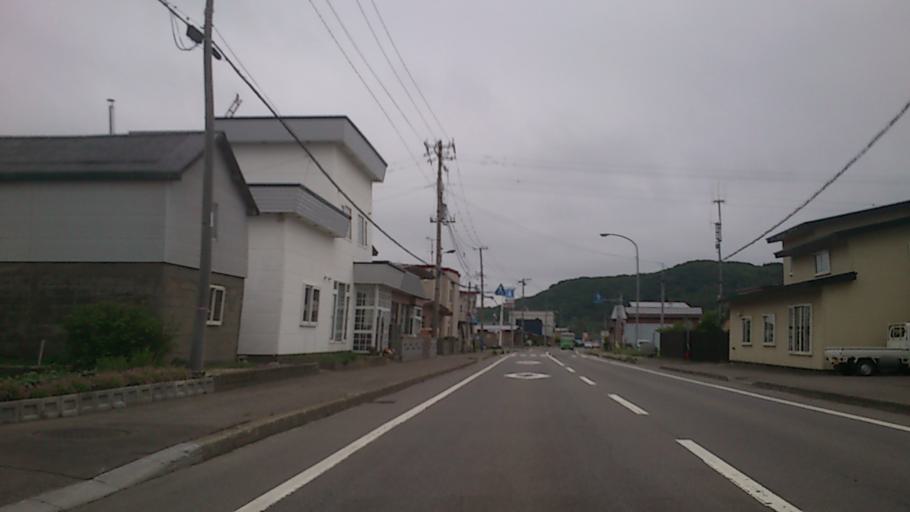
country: JP
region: Hokkaido
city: Kamiiso
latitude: 41.9772
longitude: 140.1344
